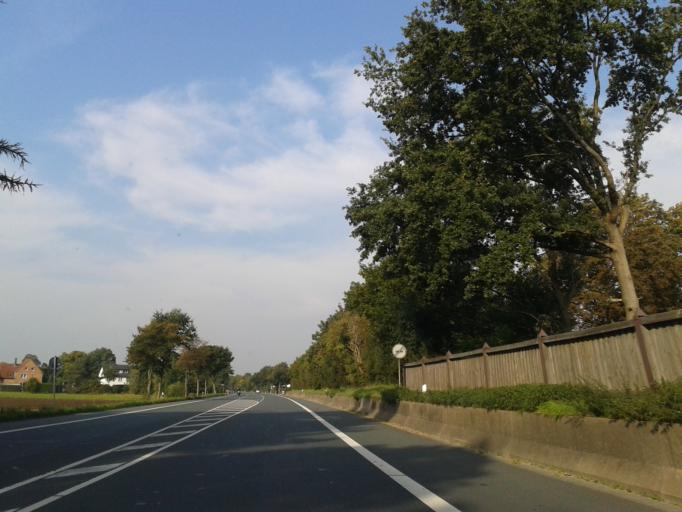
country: DE
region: North Rhine-Westphalia
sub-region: Regierungsbezirk Detmold
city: Hovelhof
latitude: 51.7597
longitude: 8.6523
